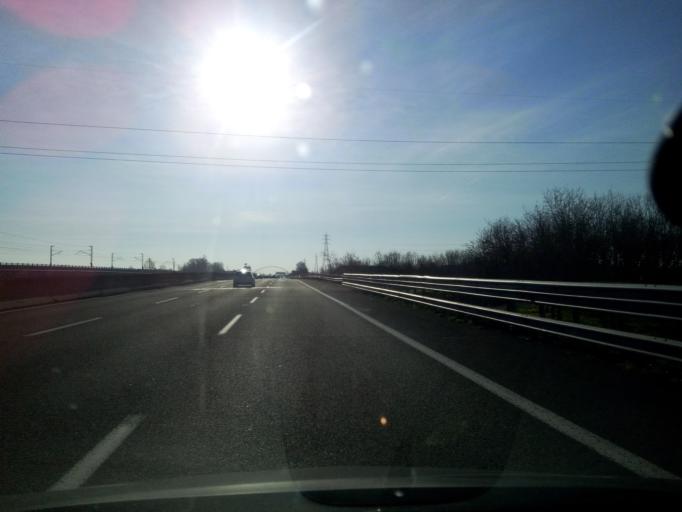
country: IT
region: Emilia-Romagna
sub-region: Provincia di Reggio Emilia
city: Roncocesi
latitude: 44.7357
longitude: 10.6005
